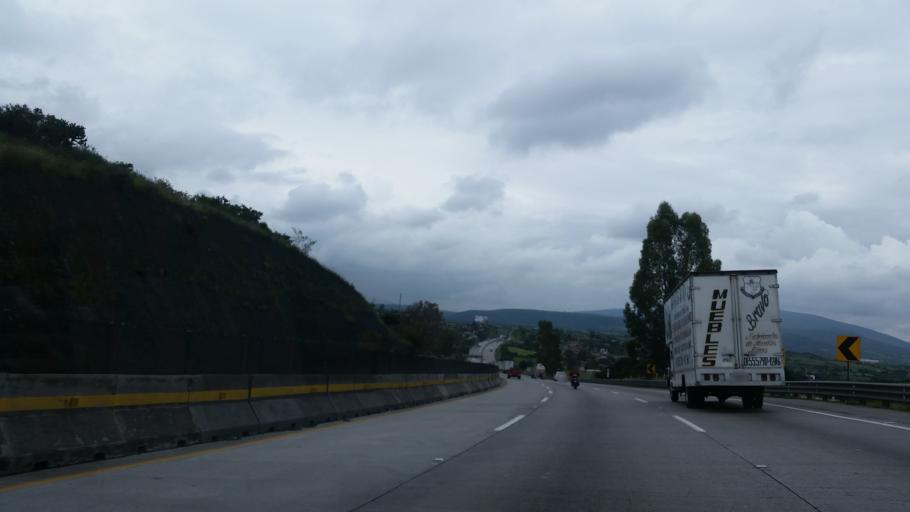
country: MX
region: Hidalgo
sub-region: Tepeji del Rio de Ocampo
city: Santiago Tlautla
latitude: 19.9329
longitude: -99.3821
